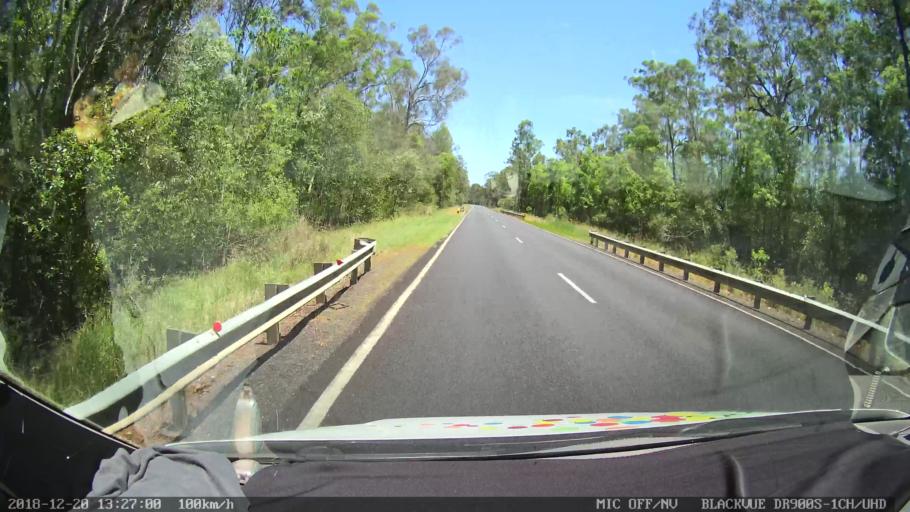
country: AU
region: New South Wales
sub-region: Richmond Valley
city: Casino
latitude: -29.1536
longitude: 152.9933
